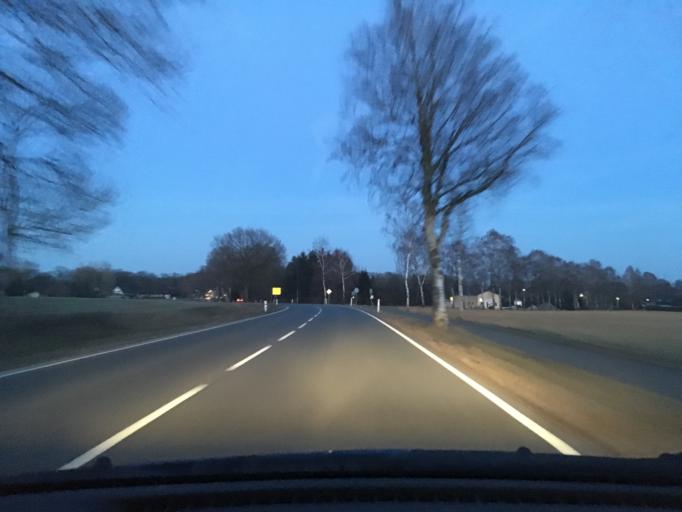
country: DE
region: Lower Saxony
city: Hemslingen
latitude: 53.0877
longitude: 9.5900
